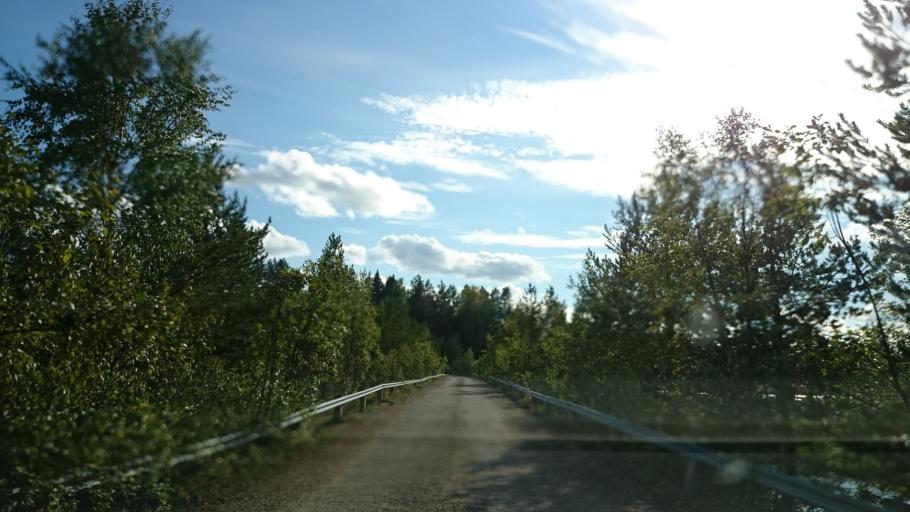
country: FI
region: Kainuu
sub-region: Kehys-Kainuu
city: Suomussalmi
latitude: 64.7374
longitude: 29.4504
